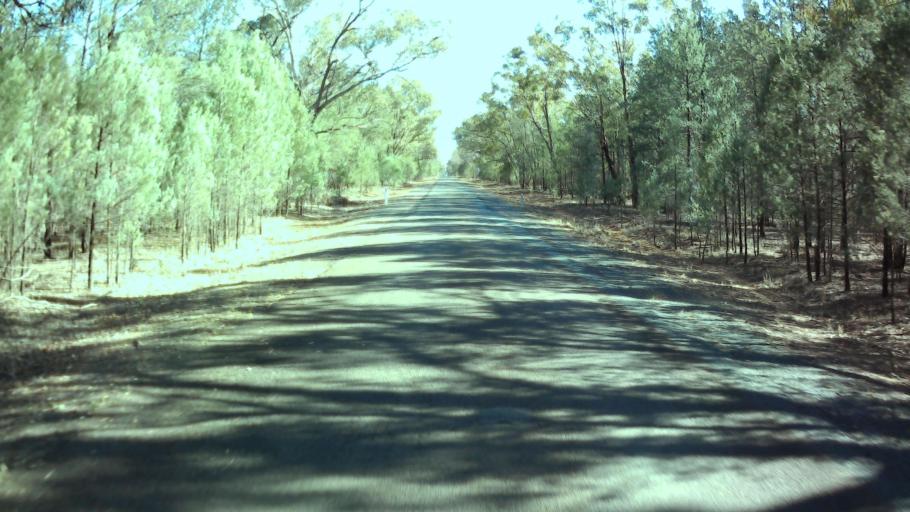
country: AU
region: New South Wales
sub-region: Weddin
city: Grenfell
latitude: -33.8120
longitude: 147.9538
